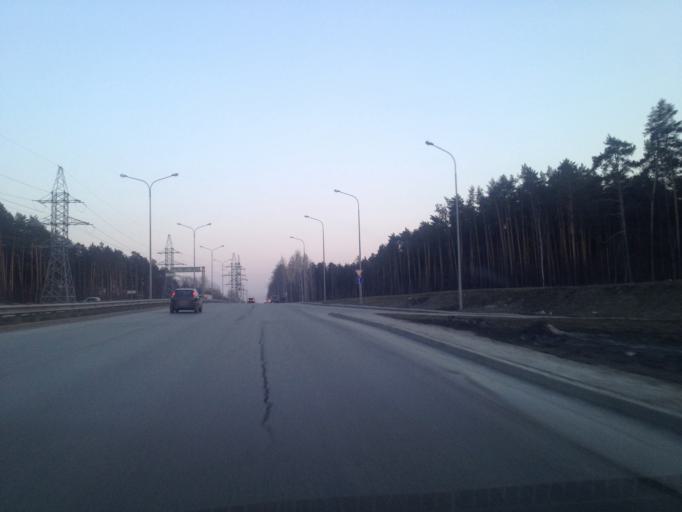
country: RU
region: Sverdlovsk
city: Sovkhoznyy
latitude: 56.7876
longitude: 60.5978
